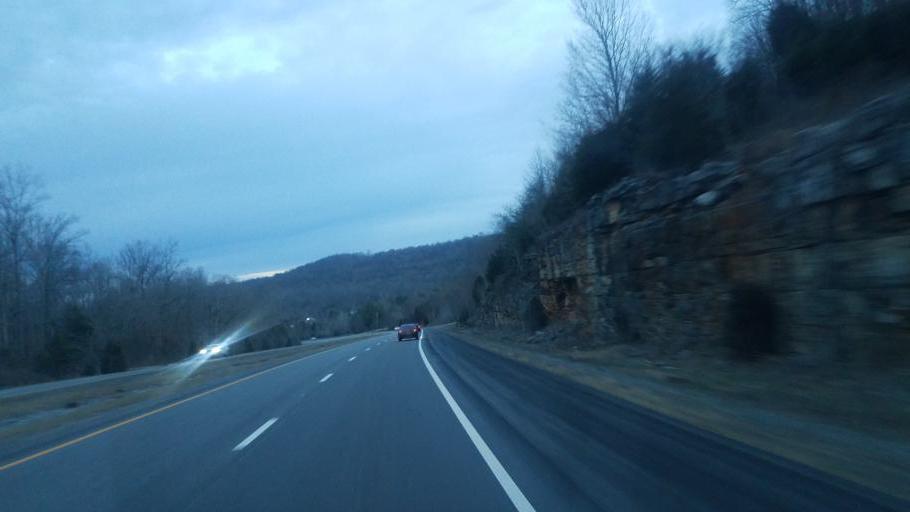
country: US
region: Tennessee
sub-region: White County
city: Sparta
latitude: 35.8554
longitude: -85.4677
